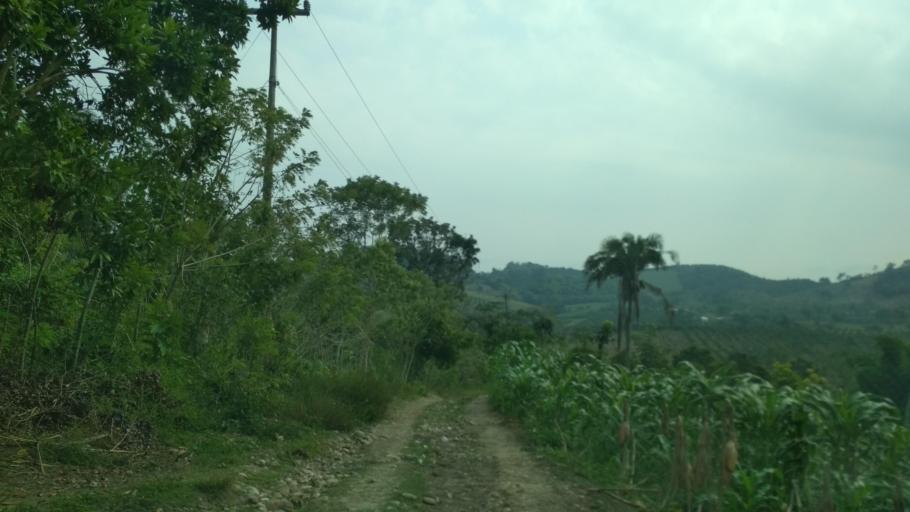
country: MM
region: Kayah
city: Loikaw
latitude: 20.2051
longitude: 97.3223
